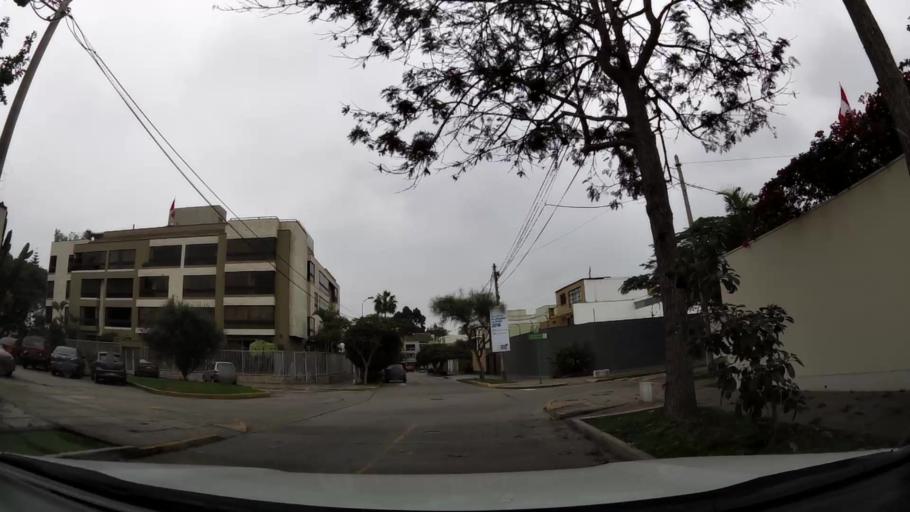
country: PE
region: Lima
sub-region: Lima
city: Surco
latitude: -12.1284
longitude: -77.0147
